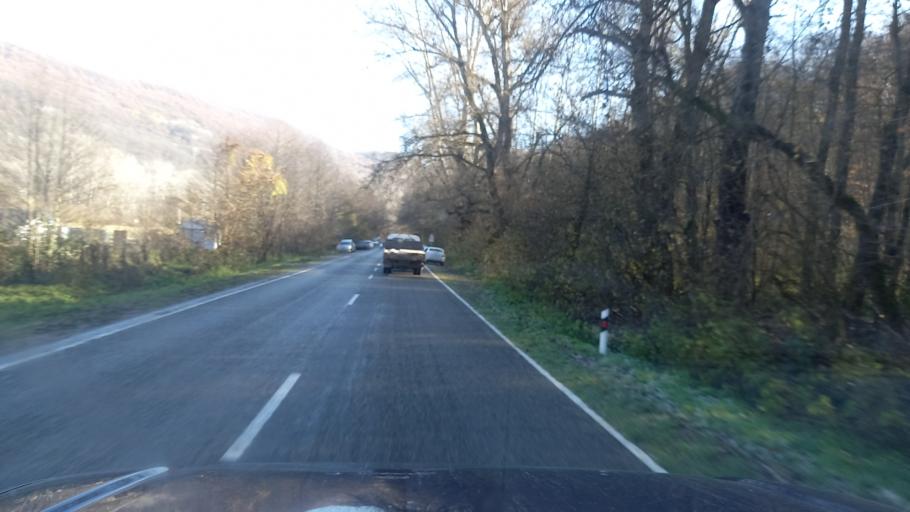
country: RU
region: Krasnodarskiy
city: Goryachiy Klyuch
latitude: 44.5970
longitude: 39.0856
